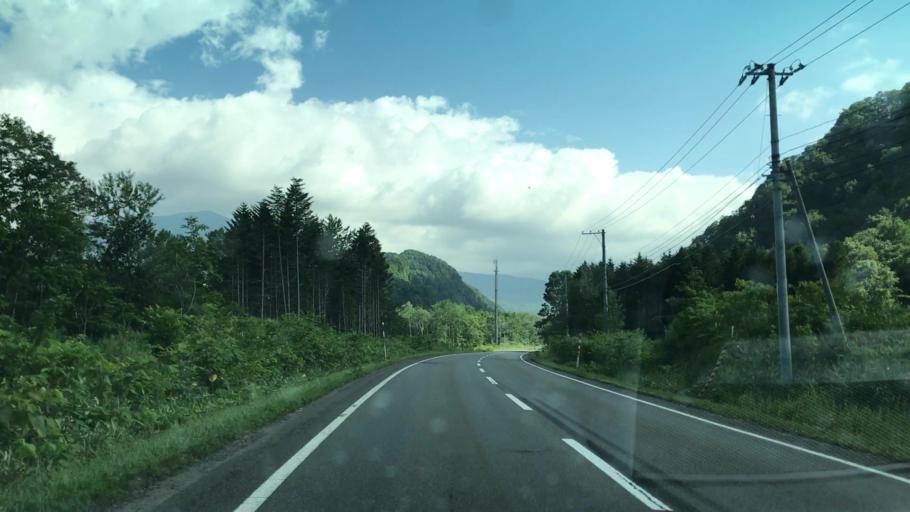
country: JP
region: Hokkaido
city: Shimo-furano
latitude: 42.8475
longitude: 142.4169
